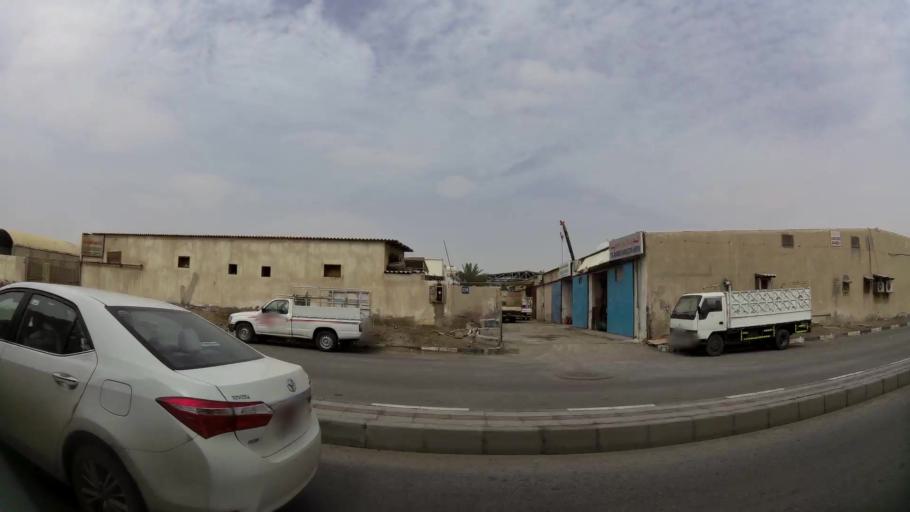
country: AE
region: Abu Dhabi
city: Abu Dhabi
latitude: 24.3548
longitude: 54.4992
